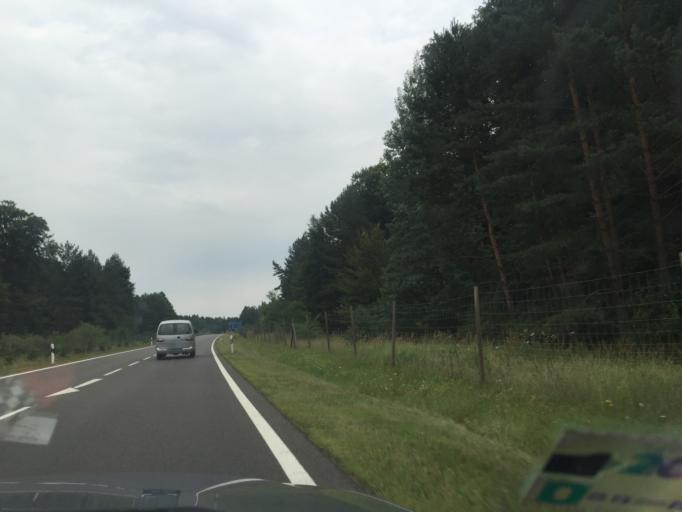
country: DE
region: Brandenburg
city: Bernau bei Berlin
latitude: 52.7293
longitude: 13.5341
